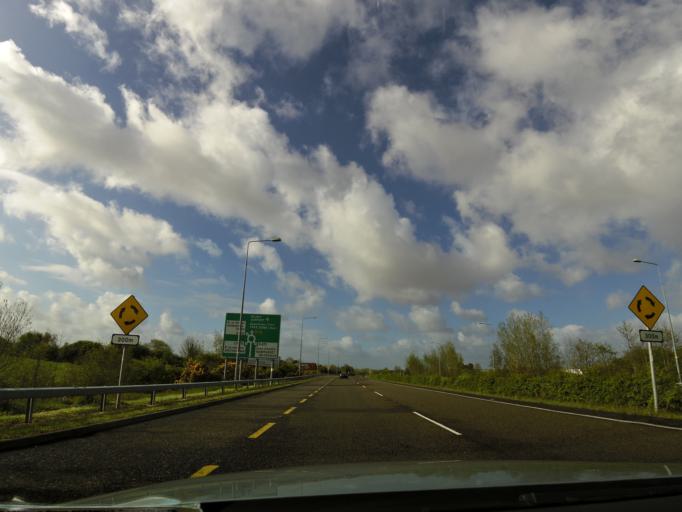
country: IE
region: Munster
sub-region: An Clar
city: Shannon
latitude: 52.7167
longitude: -8.8820
